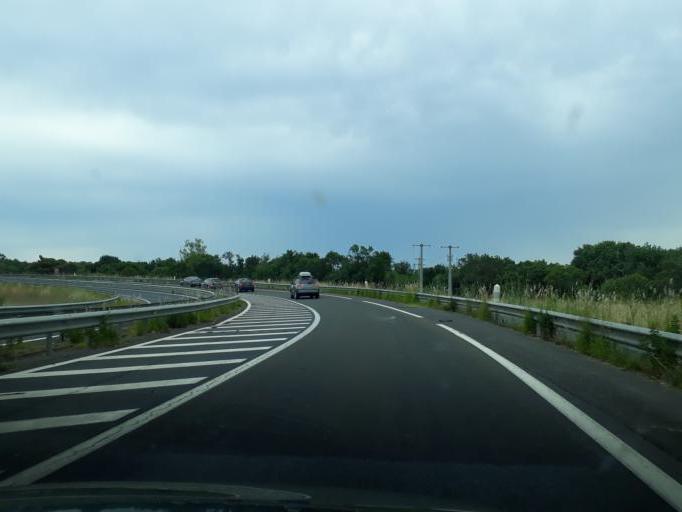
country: FR
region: Languedoc-Roussillon
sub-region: Departement de l'Herault
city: Vias
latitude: 43.3086
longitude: 3.4317
